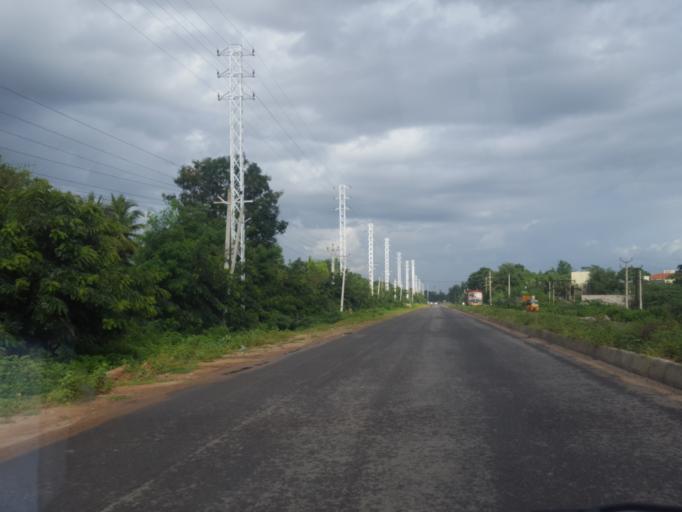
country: IN
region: Telangana
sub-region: Medak
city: Serilingampalle
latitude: 17.4024
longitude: 78.2911
